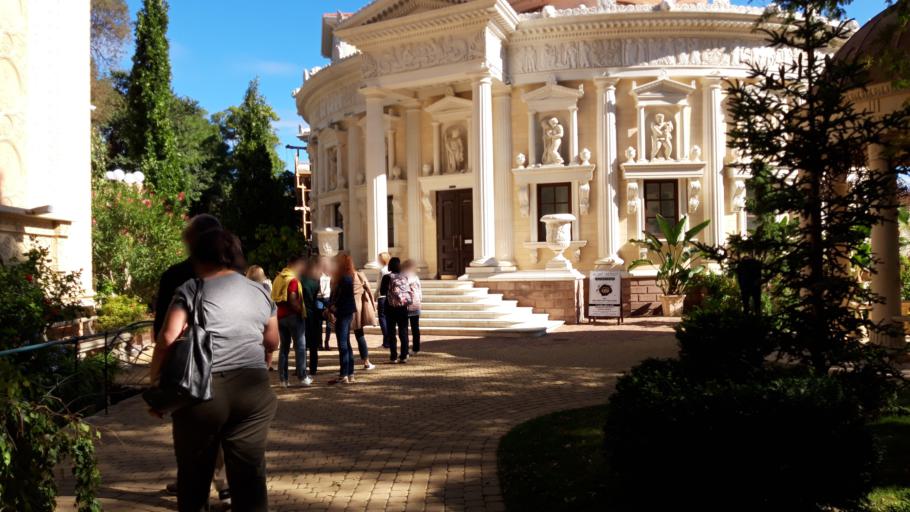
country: RU
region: Krasnodarskiy
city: Kabardinka
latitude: 44.6444
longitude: 37.9355
